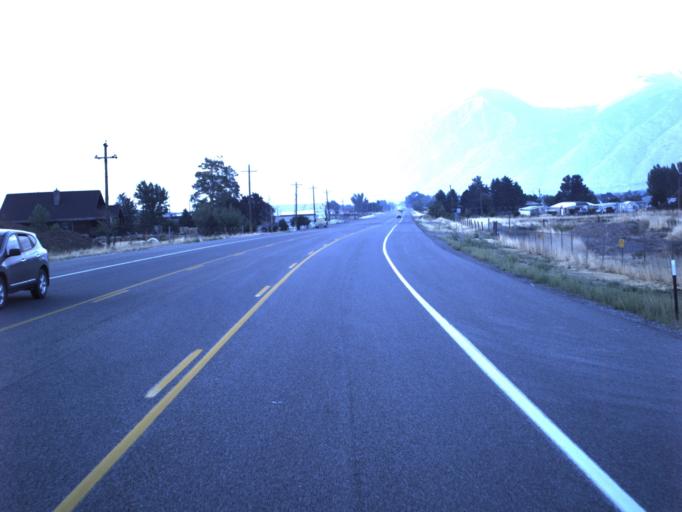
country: US
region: Utah
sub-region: Utah County
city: Mapleton
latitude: 40.1045
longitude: -111.5977
